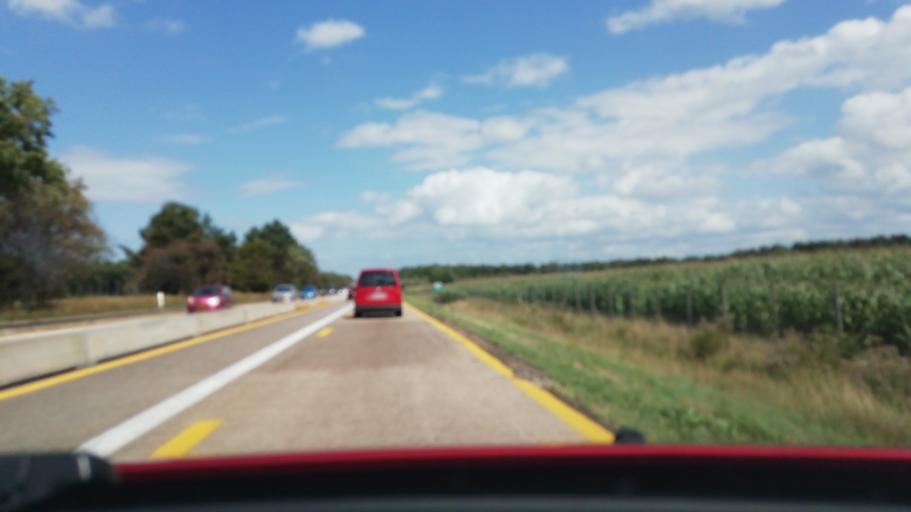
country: NL
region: North Brabant
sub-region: Gemeente Bladel en Netersel
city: Bladel
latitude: 51.3074
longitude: 5.1741
